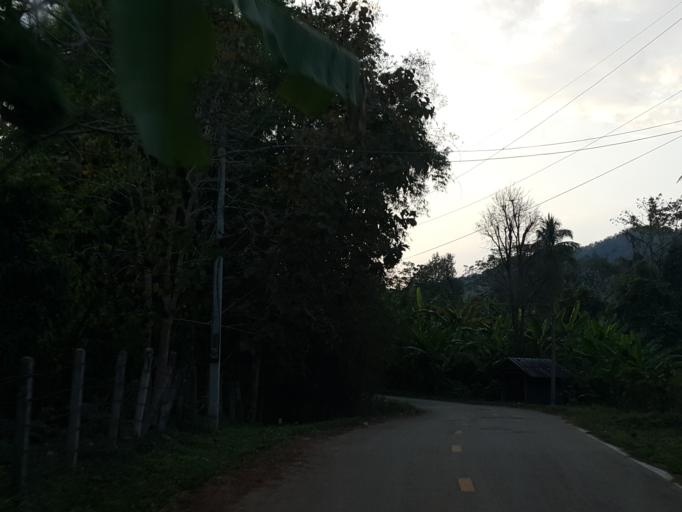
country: TH
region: Lampang
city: Mueang Pan
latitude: 18.8189
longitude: 99.4628
